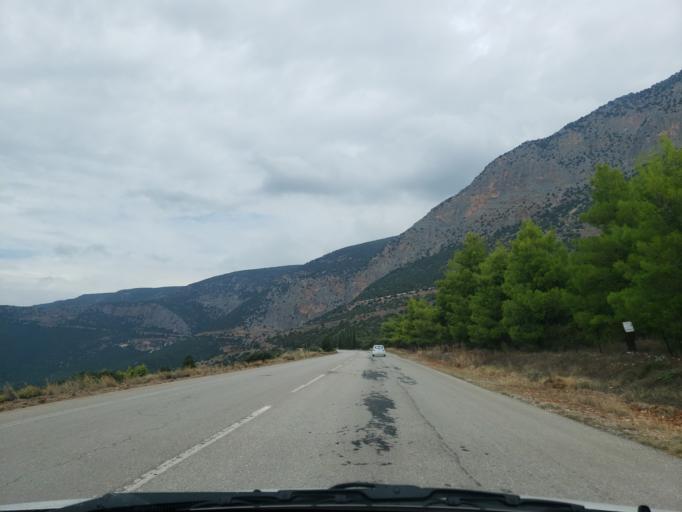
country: GR
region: Central Greece
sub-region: Nomos Fokidos
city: Delphi
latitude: 38.4853
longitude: 22.4608
